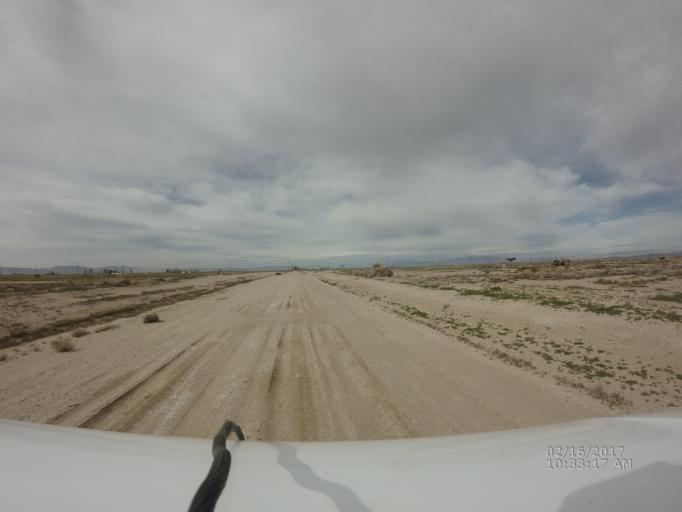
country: US
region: California
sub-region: Los Angeles County
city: Lancaster
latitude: 34.7269
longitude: -117.9648
